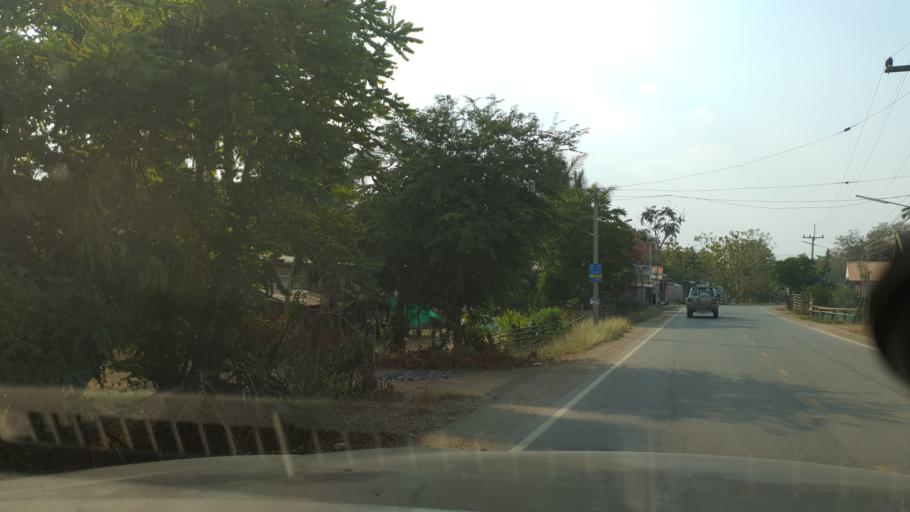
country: TH
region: Sukhothai
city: Ban Dan Lan Hoi
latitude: 17.1134
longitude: 99.5415
